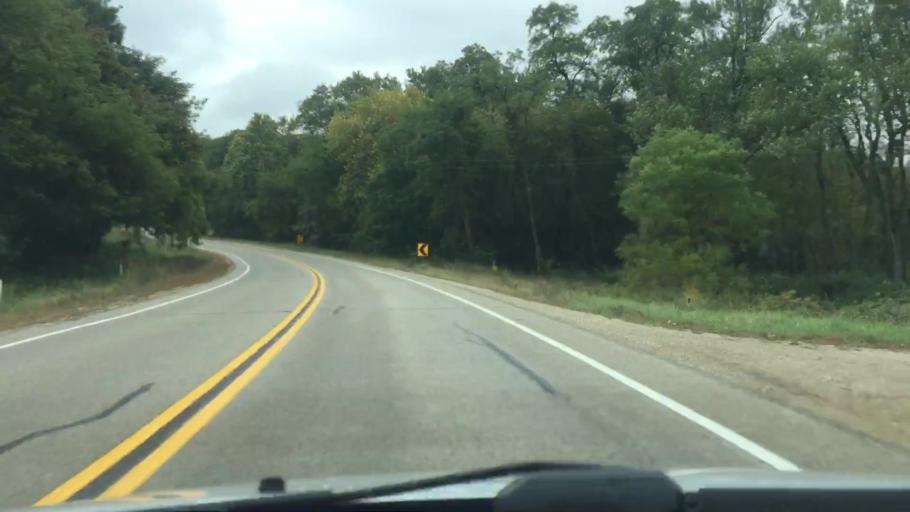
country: US
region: Wisconsin
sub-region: Waukesha County
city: Eagle
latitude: 42.9438
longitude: -88.4780
